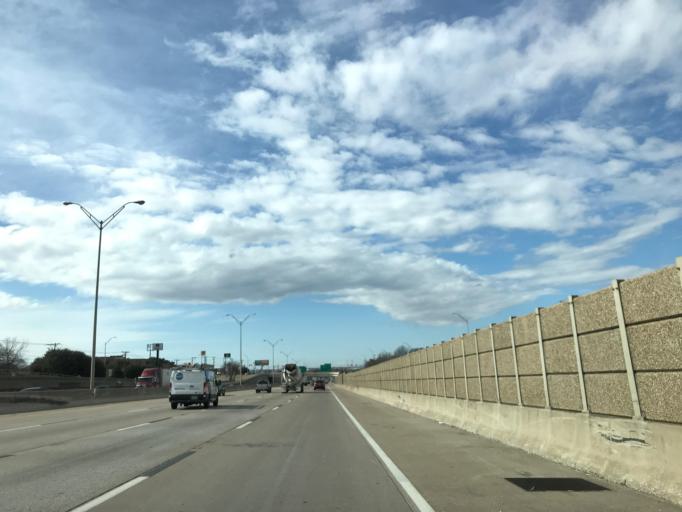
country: US
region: Texas
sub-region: Tarrant County
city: Edgecliff Village
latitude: 32.6718
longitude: -97.3709
